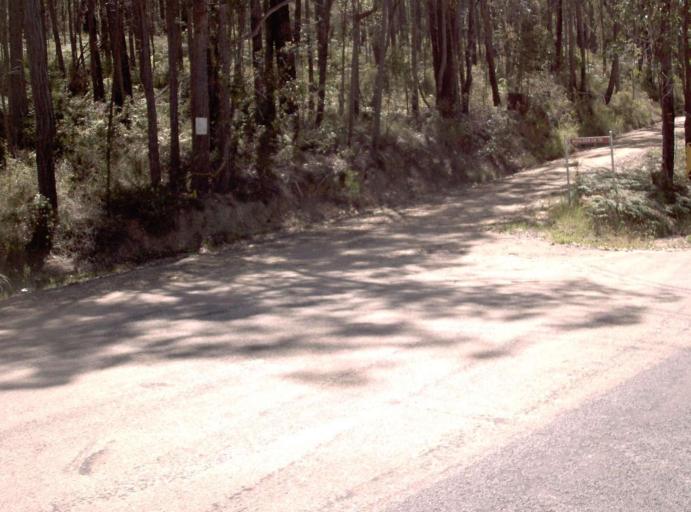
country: AU
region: New South Wales
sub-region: Bombala
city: Bombala
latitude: -37.6143
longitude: 148.8888
